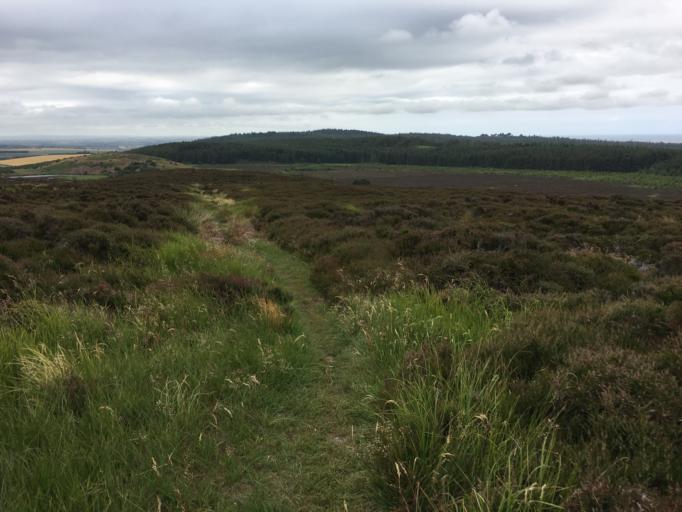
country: GB
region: England
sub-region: Northumberland
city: Lowick
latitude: 55.6173
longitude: -1.9145
